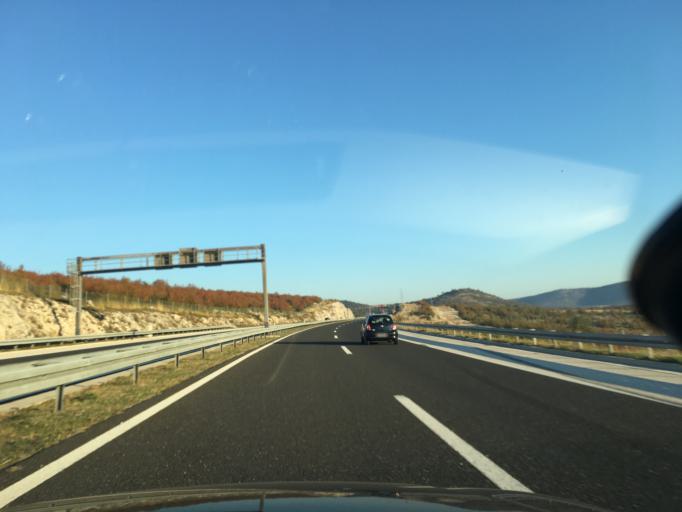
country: HR
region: Splitsko-Dalmatinska
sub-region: Grad Trogir
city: Trogir
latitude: 43.6466
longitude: 16.2004
